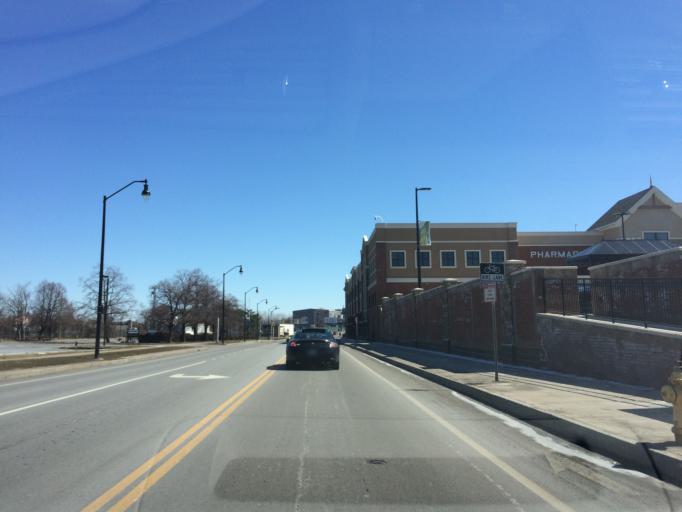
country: US
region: New York
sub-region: Monroe County
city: Brighton
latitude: 43.1470
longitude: -77.5572
